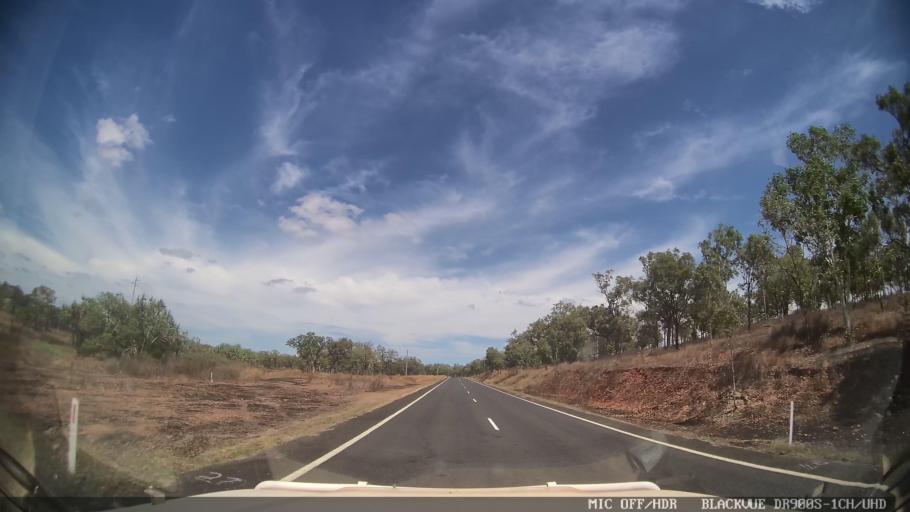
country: AU
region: Queensland
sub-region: Cook
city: Cooktown
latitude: -15.7972
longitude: 144.9258
